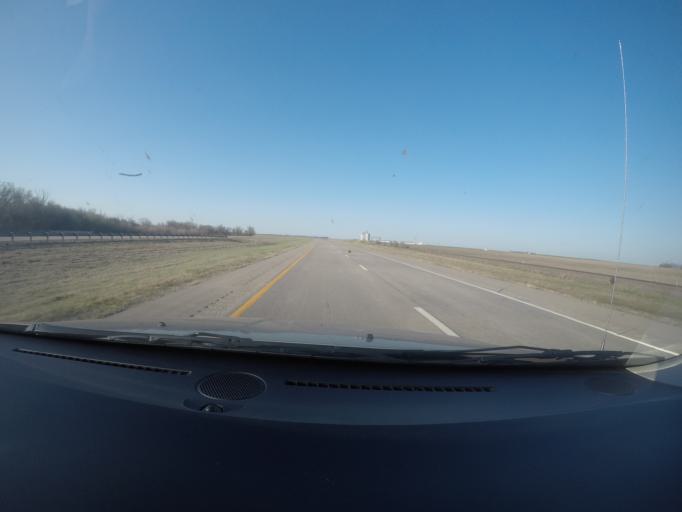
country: US
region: Kansas
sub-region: McPherson County
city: Inman
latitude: 38.2826
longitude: -97.7395
